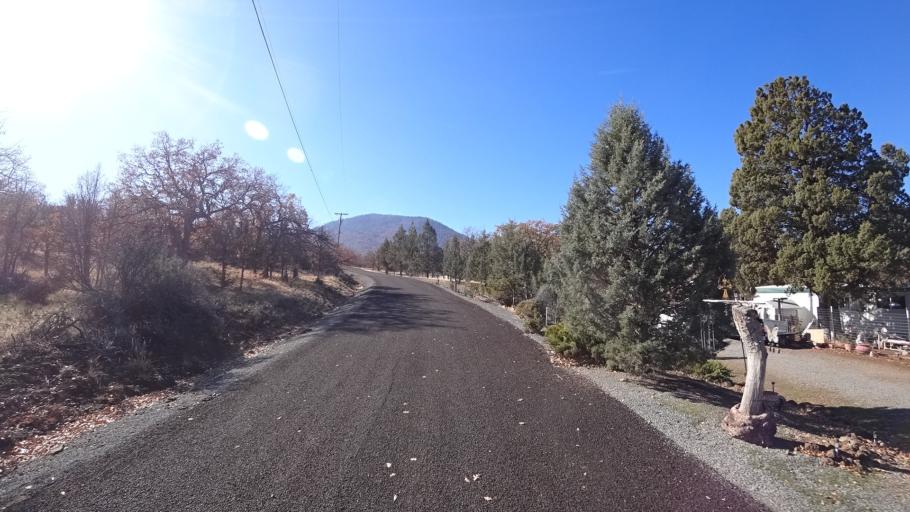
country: US
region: California
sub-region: Siskiyou County
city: Montague
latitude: 41.8862
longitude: -122.4829
